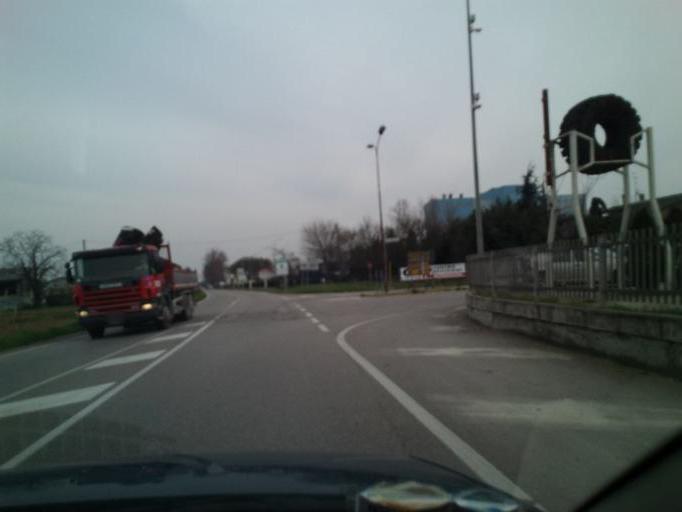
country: IT
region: Veneto
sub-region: Provincia di Verona
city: Mozzecane
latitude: 45.3158
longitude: 10.8244
